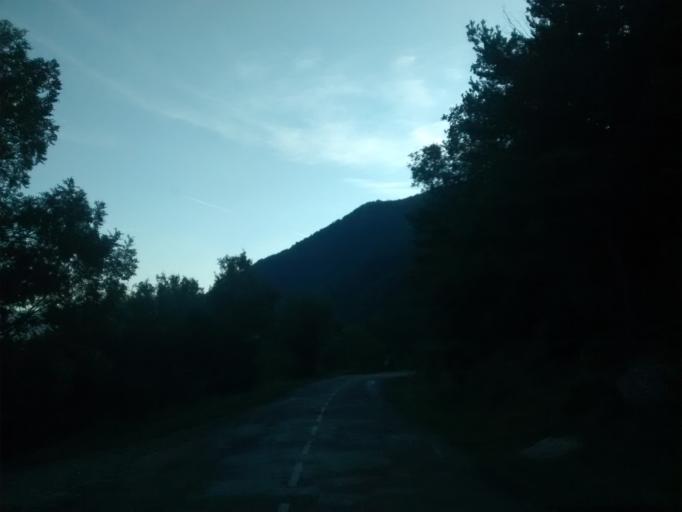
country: ES
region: Aragon
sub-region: Provincia de Huesca
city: Anso
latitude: 42.7820
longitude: -0.7385
